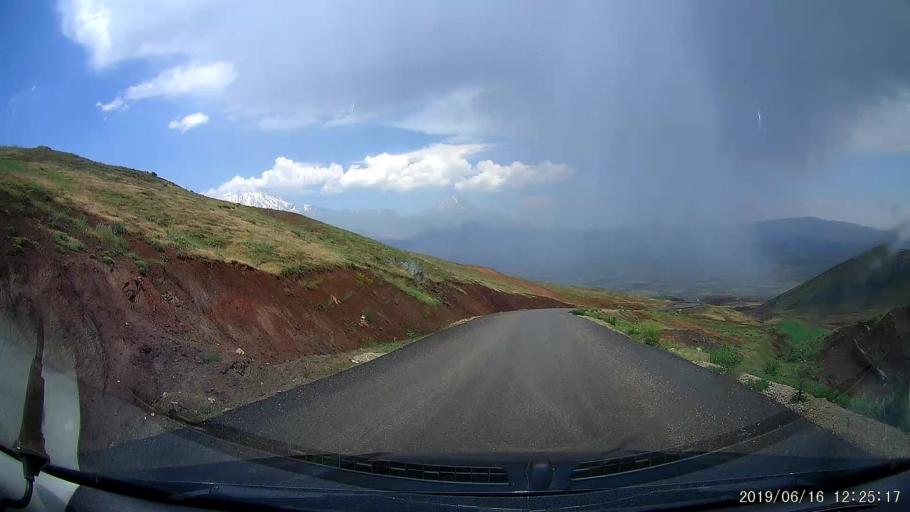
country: TR
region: Agri
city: Dogubayazit
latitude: 39.4433
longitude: 44.2341
